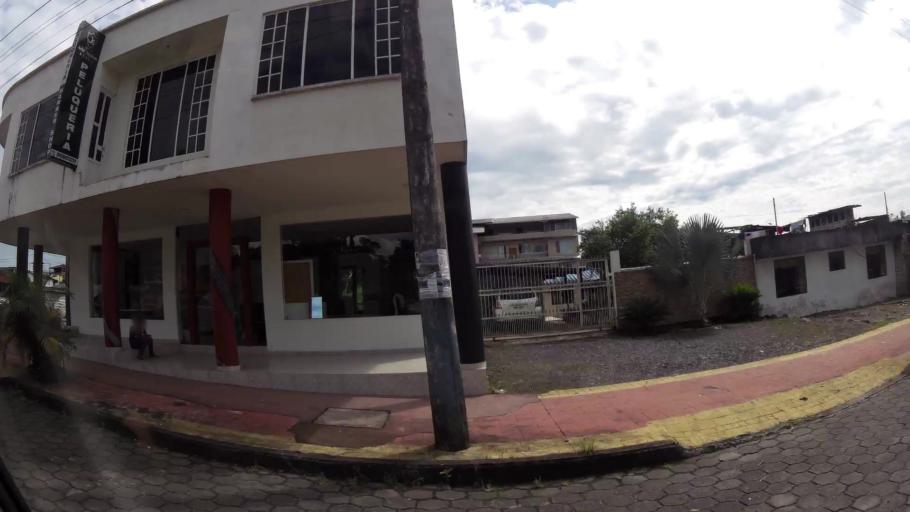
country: EC
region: Pastaza
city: Puyo
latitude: -1.4869
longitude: -78.0085
